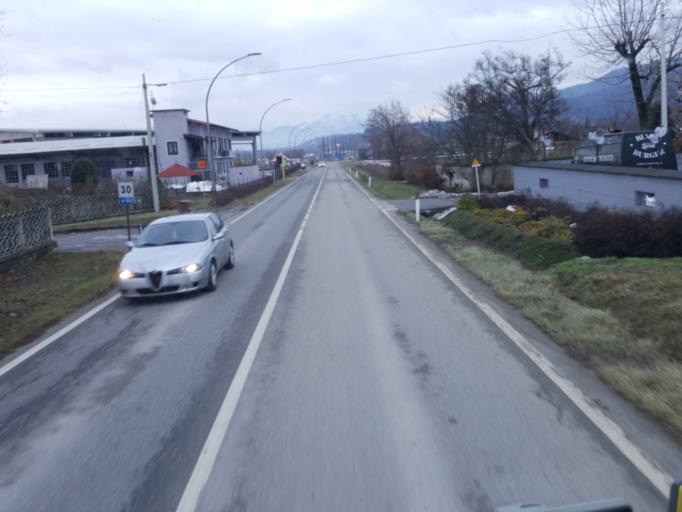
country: IT
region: Piedmont
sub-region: Provincia di Cuneo
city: Caraglio
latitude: 44.4042
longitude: 7.4458
